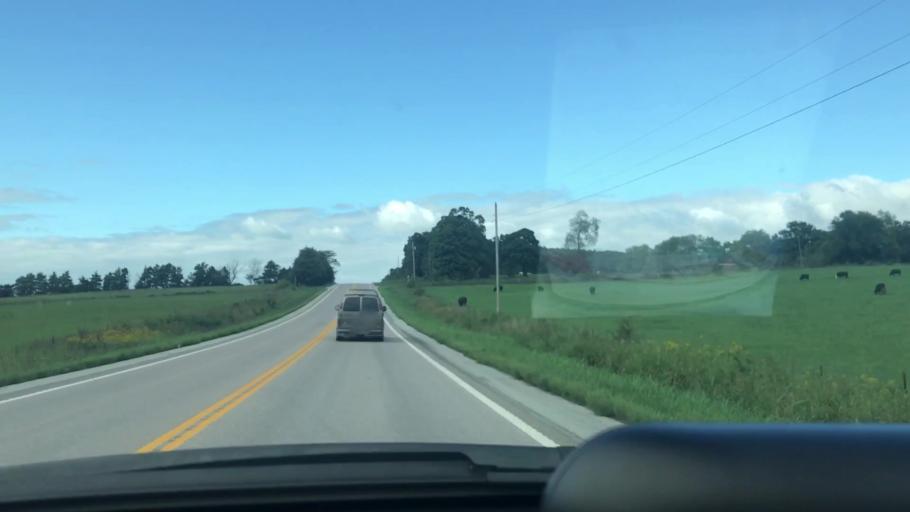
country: US
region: Missouri
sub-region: Hickory County
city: Hermitage
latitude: 37.9609
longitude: -93.2069
